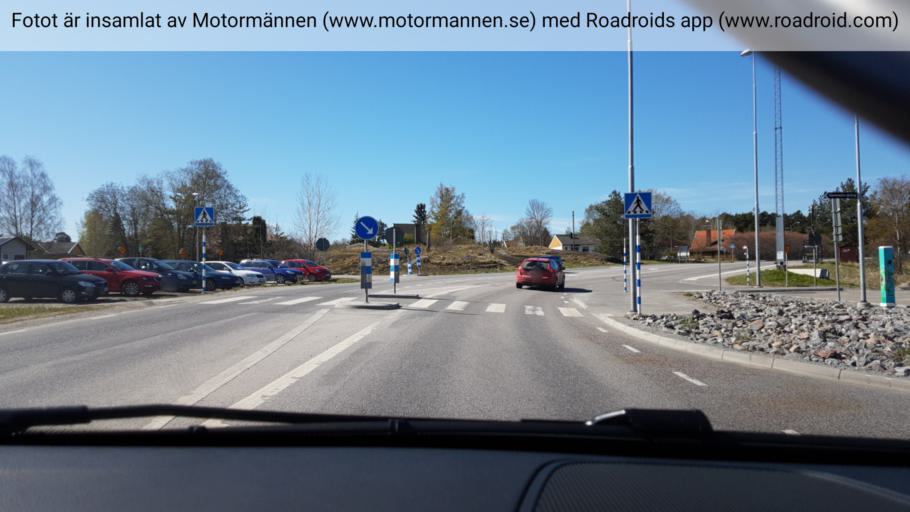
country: SE
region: Stockholm
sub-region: Varmdo Kommun
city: Hemmesta
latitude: 59.3271
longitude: 18.5042
